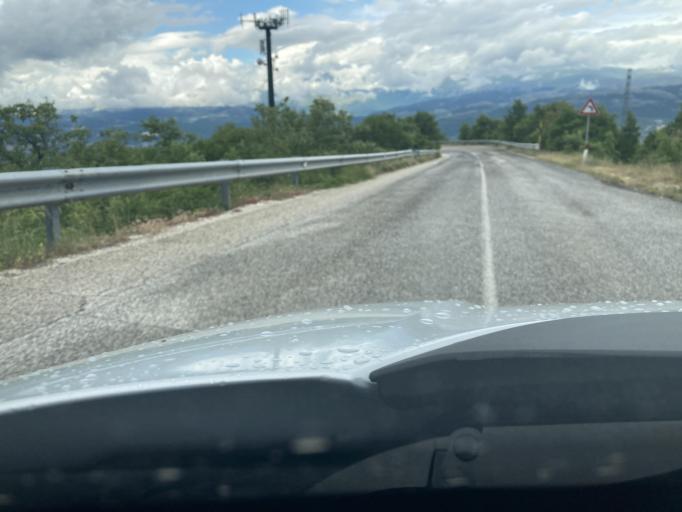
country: IT
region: Abruzzo
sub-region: Provincia dell' Aquila
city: San Panfilo d'Ocre
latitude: 42.2726
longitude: 13.4851
